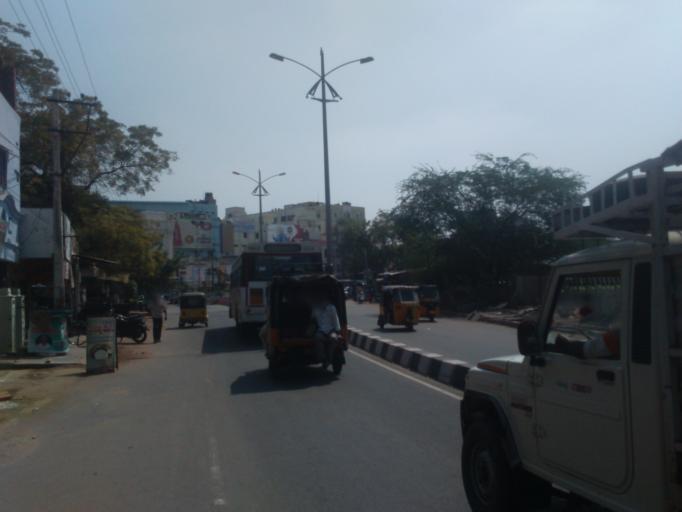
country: IN
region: Telangana
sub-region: Mahbubnagar
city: Alampur
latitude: 15.8389
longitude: 78.0400
